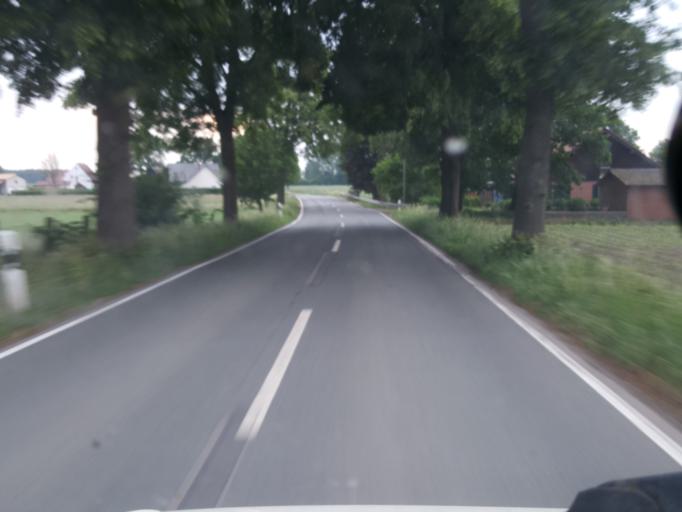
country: DE
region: North Rhine-Westphalia
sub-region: Regierungsbezirk Detmold
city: Petershagen
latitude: 52.3700
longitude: 8.8770
